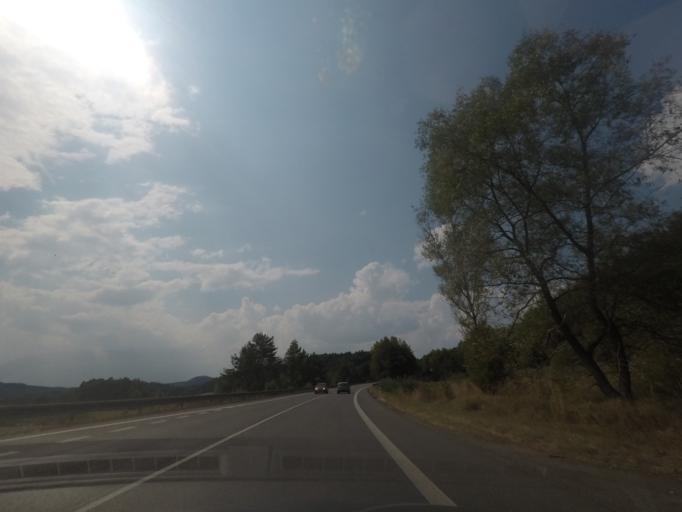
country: CZ
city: Cvikov
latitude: 50.7720
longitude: 14.6695
